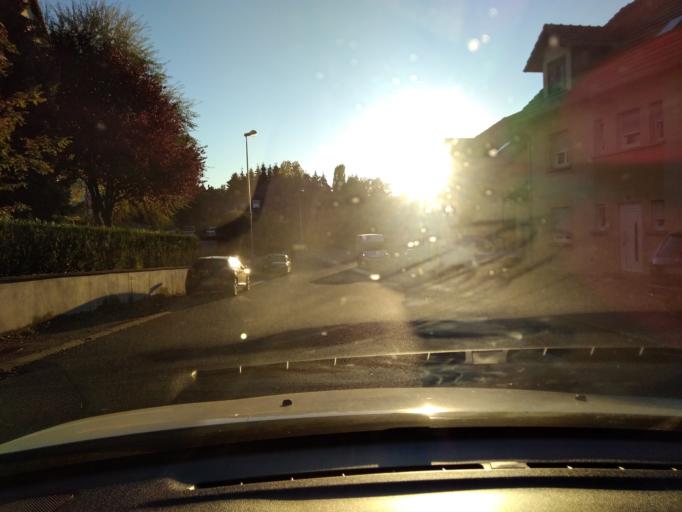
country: FR
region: Lorraine
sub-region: Departement de la Moselle
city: Sarreguemines
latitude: 49.1021
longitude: 7.0538
